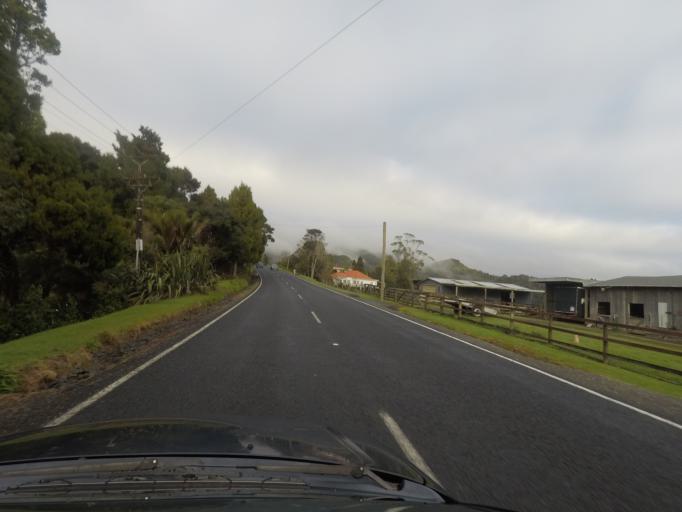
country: NZ
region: Auckland
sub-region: Auckland
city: Waitakere
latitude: -36.9179
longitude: 174.5883
